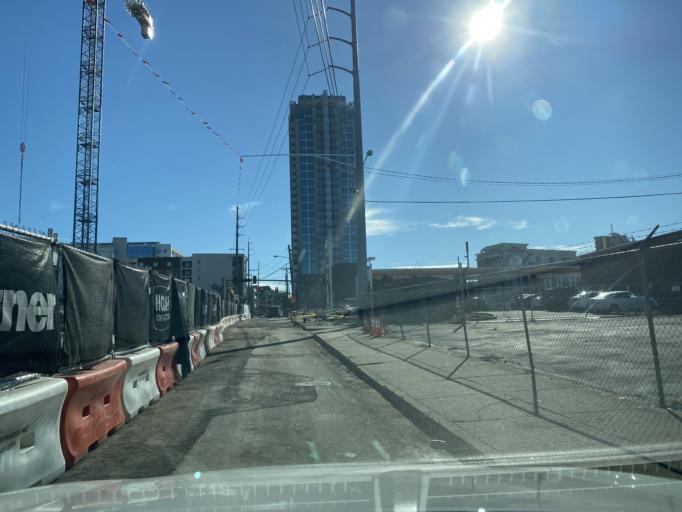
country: US
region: Tennessee
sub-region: Davidson County
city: Nashville
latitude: 36.1545
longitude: -86.7950
